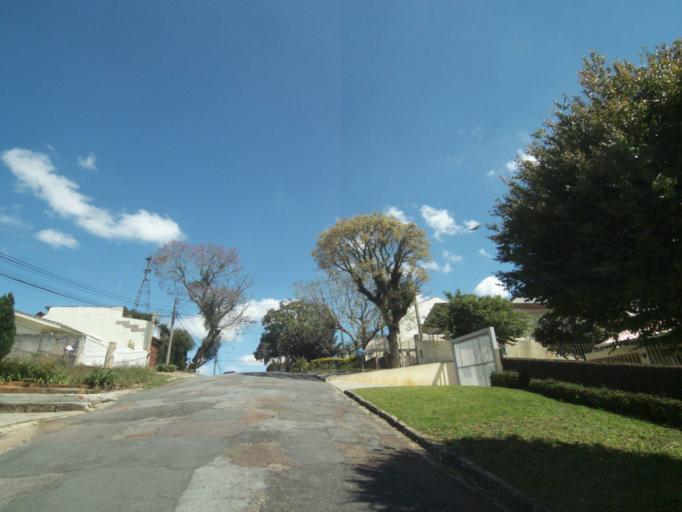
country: BR
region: Parana
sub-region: Curitiba
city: Curitiba
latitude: -25.3998
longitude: -49.2733
